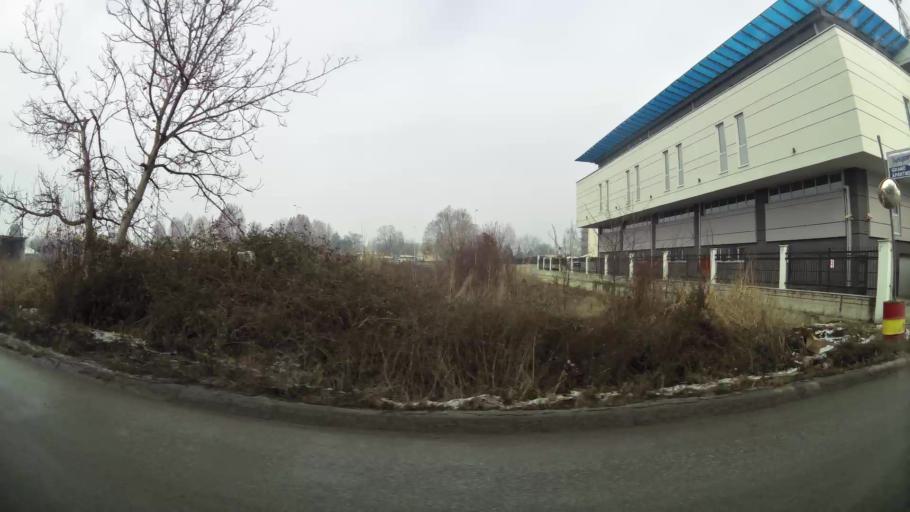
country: MK
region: Ilinden
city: Jurumleri
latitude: 41.9949
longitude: 21.5516
